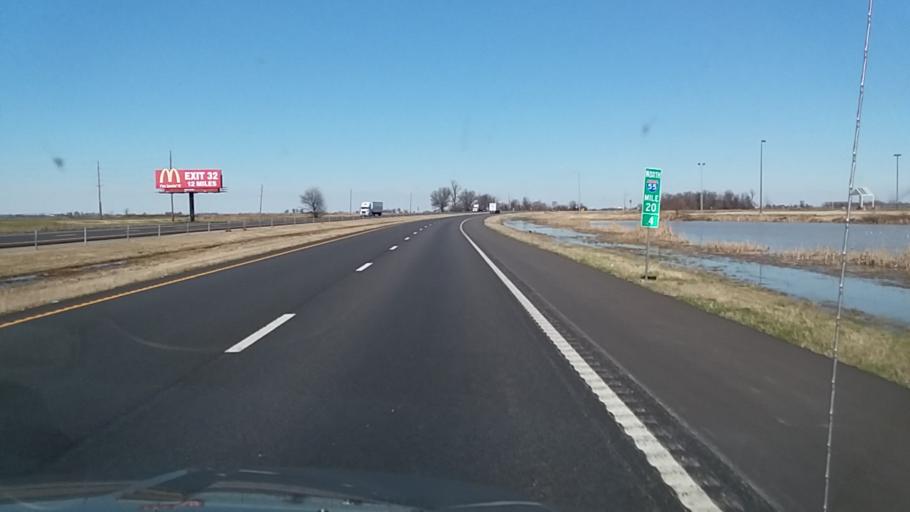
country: US
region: Missouri
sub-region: Pemiscot County
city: Hayti
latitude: 36.2504
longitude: -89.7287
